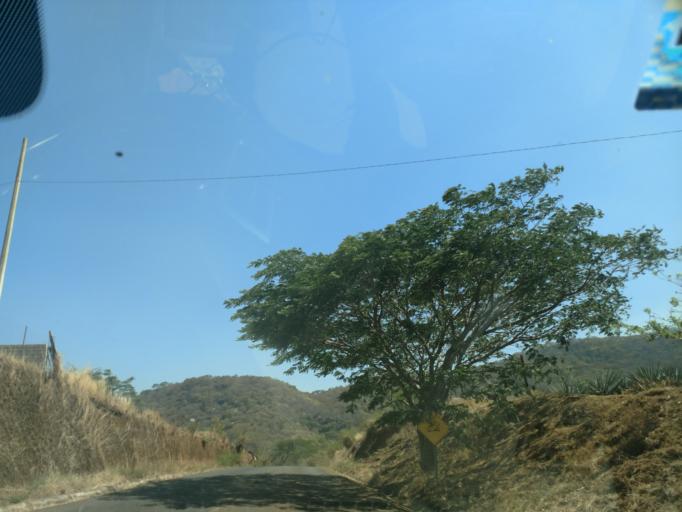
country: MX
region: Nayarit
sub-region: Tepic
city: La Corregidora
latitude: 21.4846
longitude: -104.6775
